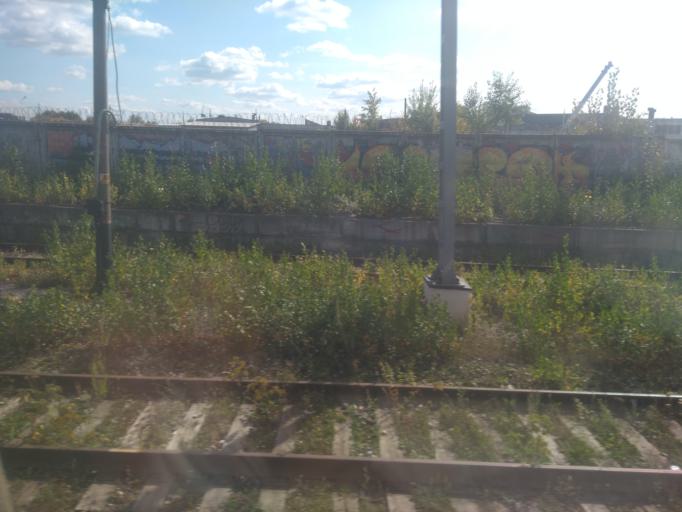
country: RU
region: Tatarstan
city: Verkhniy Uslon
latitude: 55.8054
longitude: 49.0448
